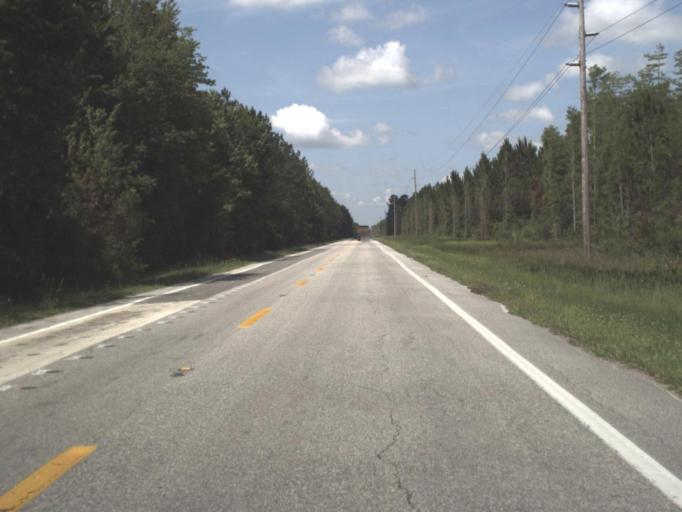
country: US
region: Florida
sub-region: Levy County
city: Bronson
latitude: 29.3733
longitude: -82.7179
